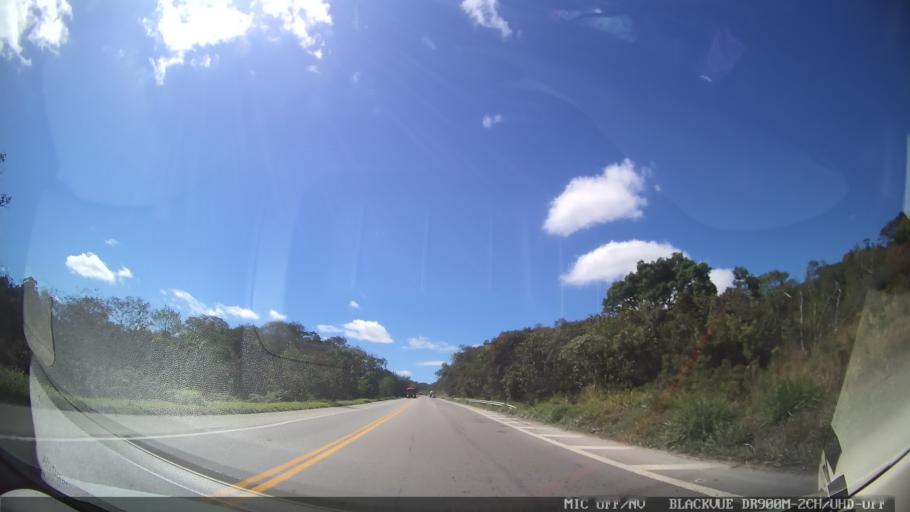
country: BR
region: Sao Paulo
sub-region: Campo Limpo Paulista
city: Campo Limpo Paulista
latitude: -23.1950
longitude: -46.7901
